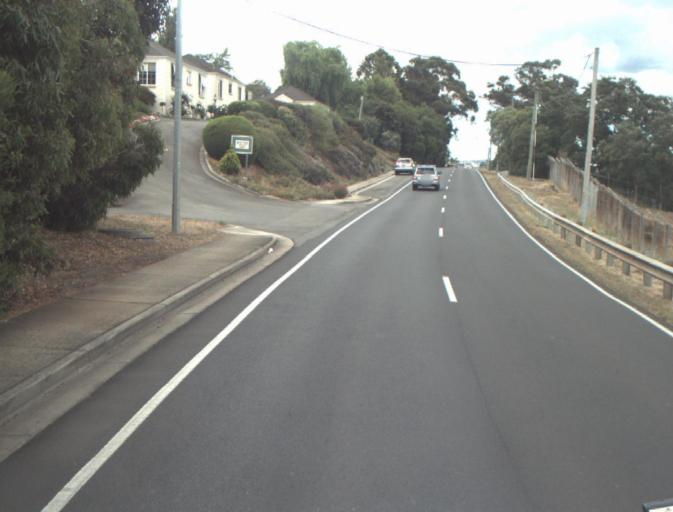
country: AU
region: Tasmania
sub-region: Launceston
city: Launceston
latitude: -41.4231
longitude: 147.1114
